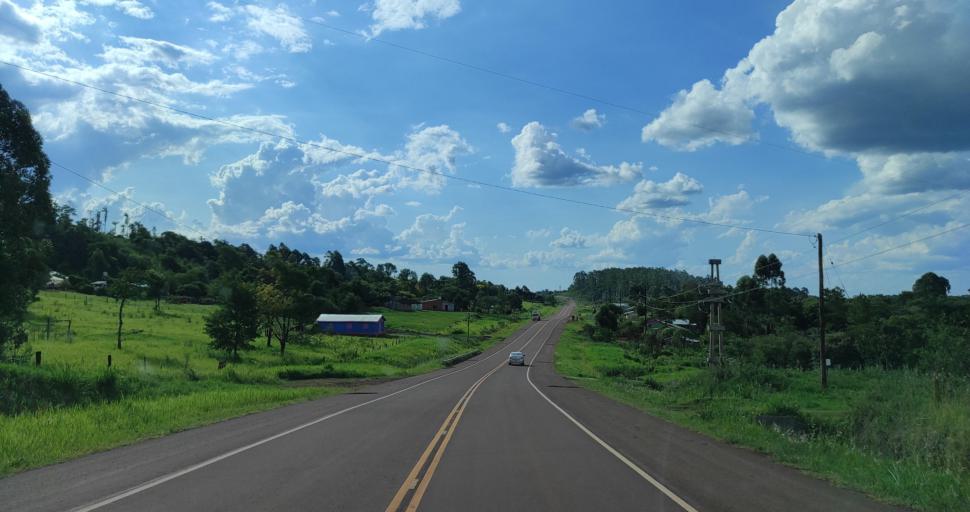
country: AR
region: Misiones
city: Bernardo de Irigoyen
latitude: -26.3859
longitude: -53.9124
